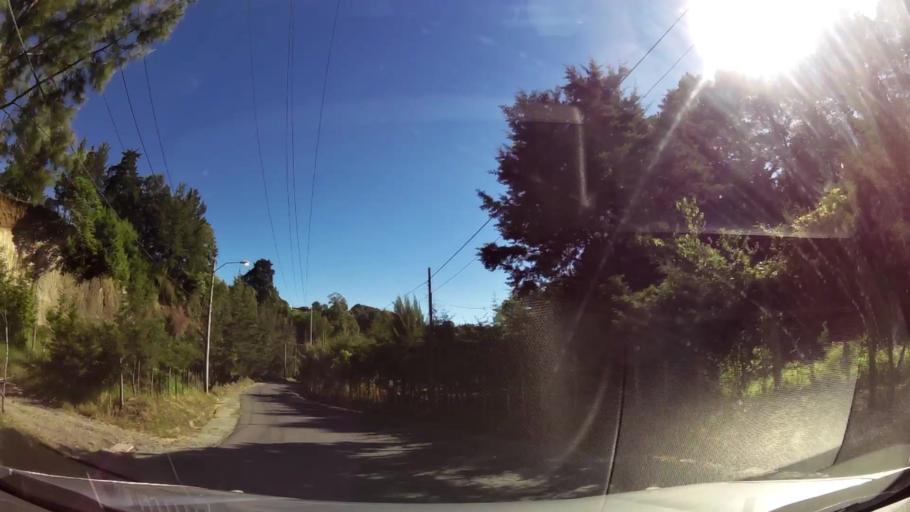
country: GT
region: Guatemala
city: Fraijanes
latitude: 14.4546
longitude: -90.4414
